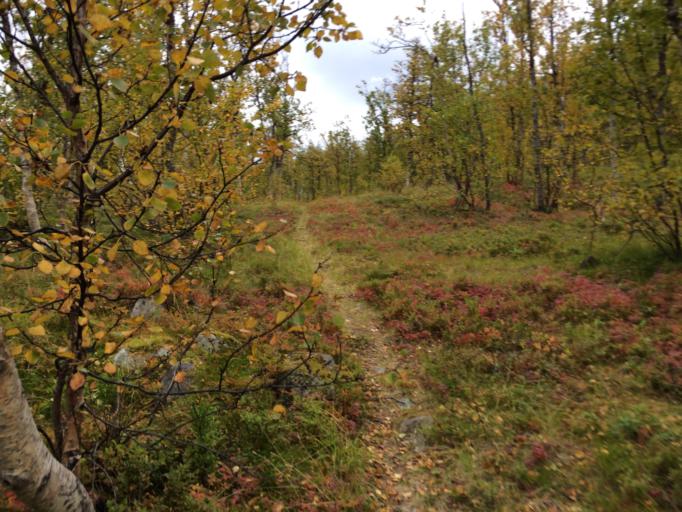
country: NO
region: Troms
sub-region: Sorreisa
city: Sorreisa
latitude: 69.5357
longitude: 18.3120
